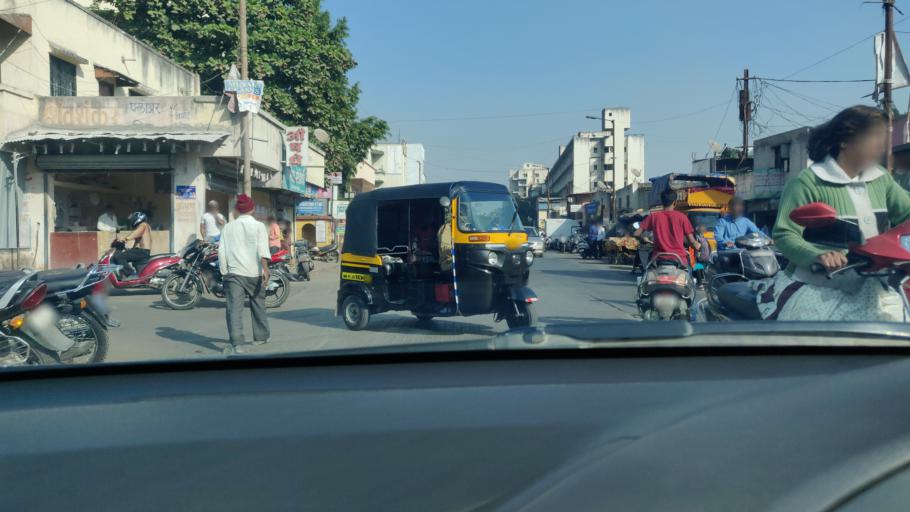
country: IN
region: Maharashtra
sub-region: Pune Division
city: Khadki
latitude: 18.5607
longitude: 73.8030
